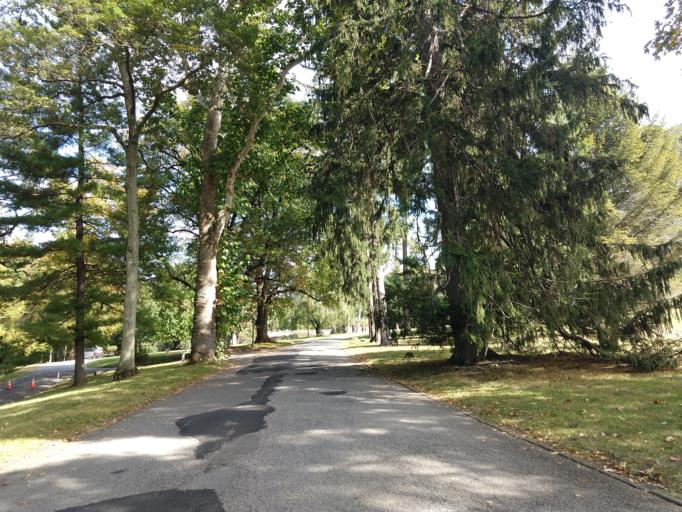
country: US
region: New York
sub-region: Westchester County
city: Irvington
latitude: 41.0543
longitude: -73.8670
